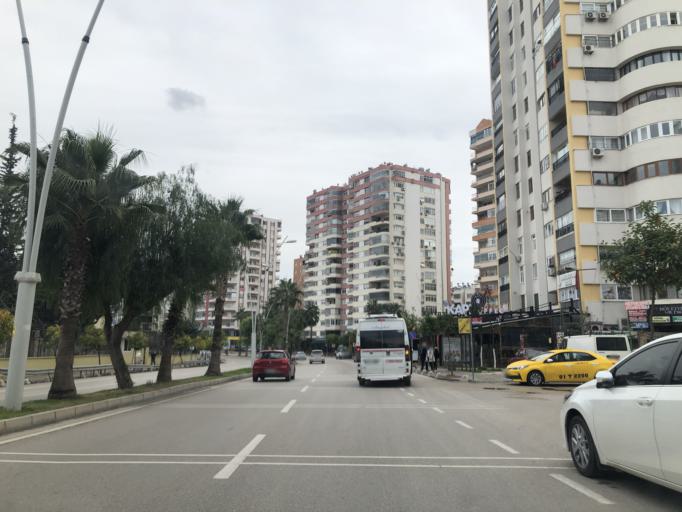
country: TR
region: Adana
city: Adana
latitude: 37.0527
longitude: 35.2917
